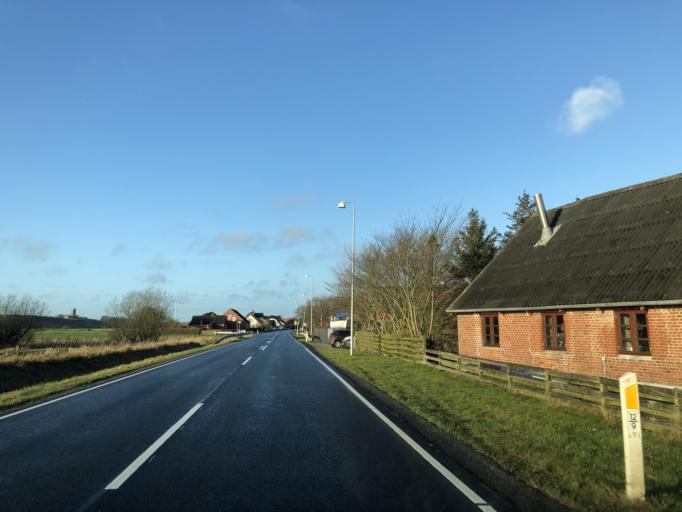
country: DK
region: Central Jutland
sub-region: Struer Kommune
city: Struer
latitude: 56.5479
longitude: 8.4912
